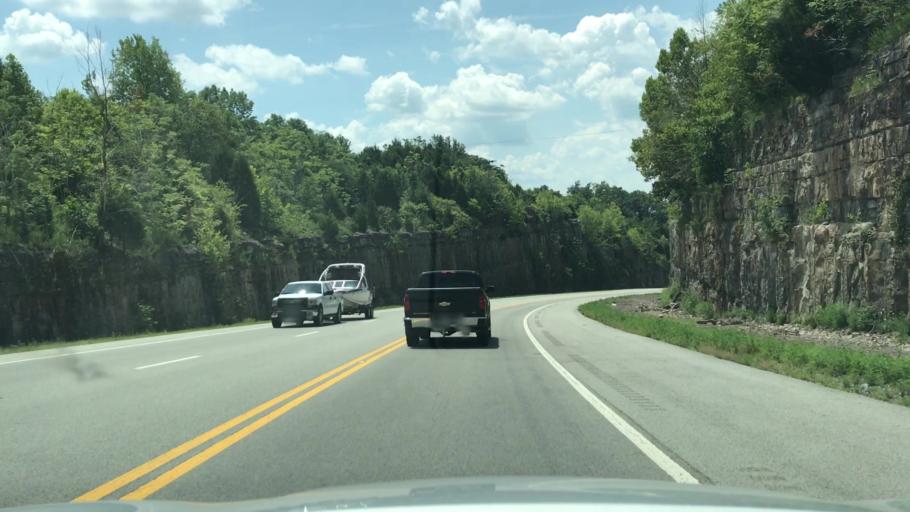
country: US
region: Tennessee
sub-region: Pickett County
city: Byrdstown
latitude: 36.5399
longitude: -85.1601
